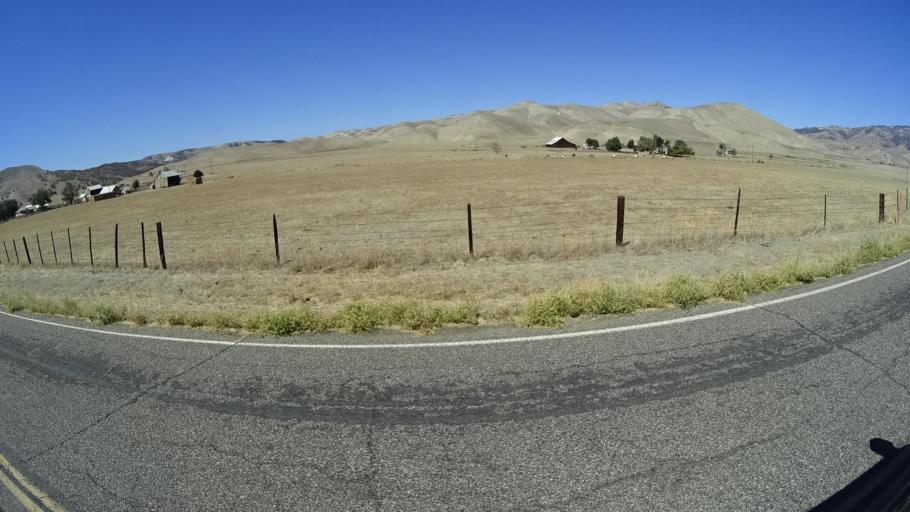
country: US
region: California
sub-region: Monterey County
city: King City
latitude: 36.2779
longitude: -120.9408
